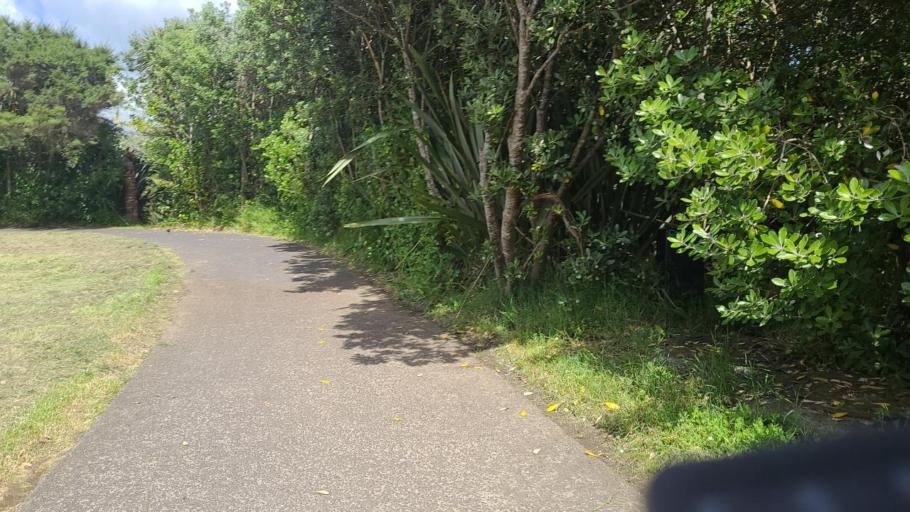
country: NZ
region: Auckland
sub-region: Auckland
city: Rosebank
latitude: -36.8630
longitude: 174.6381
